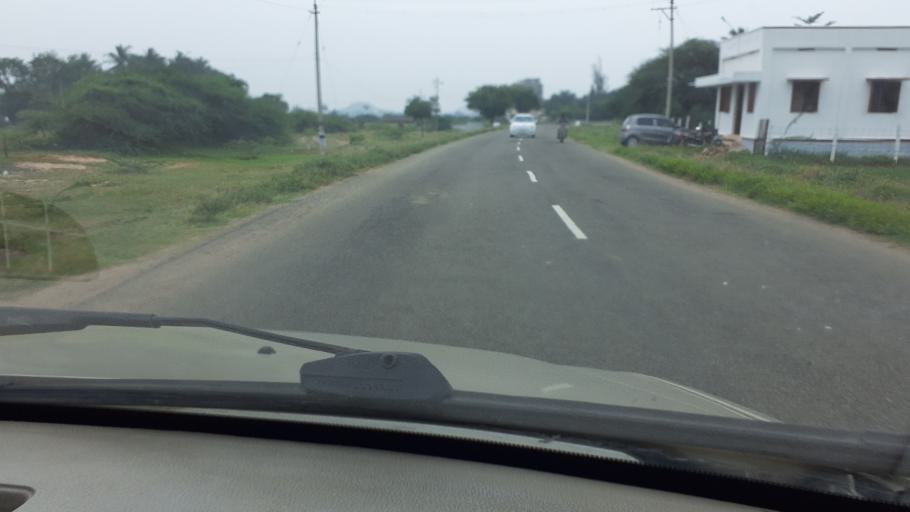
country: IN
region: Tamil Nadu
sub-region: Tirunelveli Kattabo
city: Nanguneri
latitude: 8.4857
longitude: 77.6464
